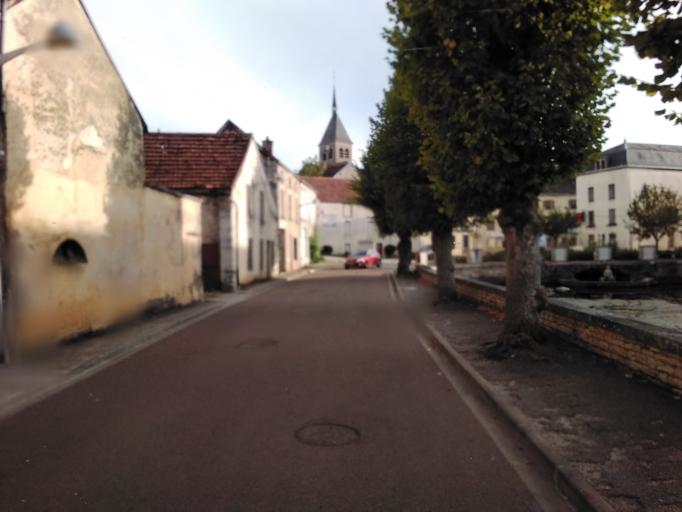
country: FR
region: Champagne-Ardenne
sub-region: Departement de l'Aube
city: Les Riceys
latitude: 47.8433
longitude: 4.3656
